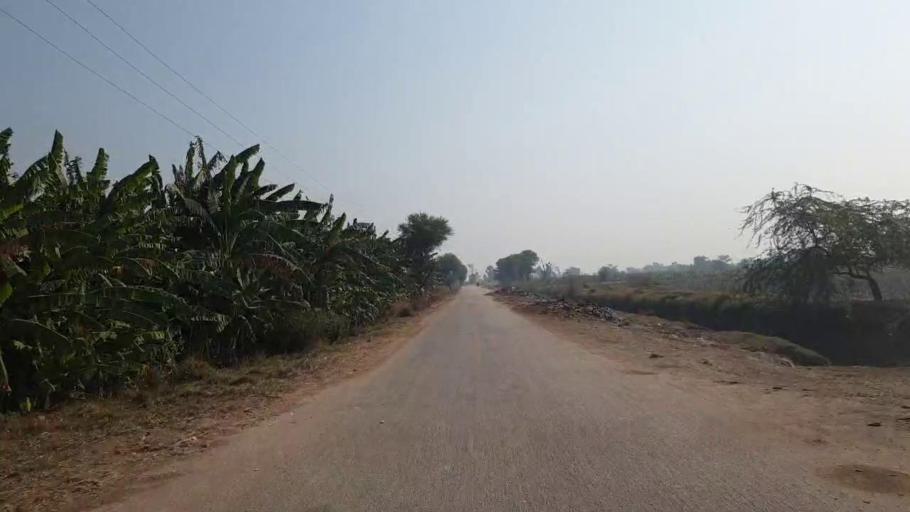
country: PK
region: Sindh
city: Hala
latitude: 25.9590
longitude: 68.4136
